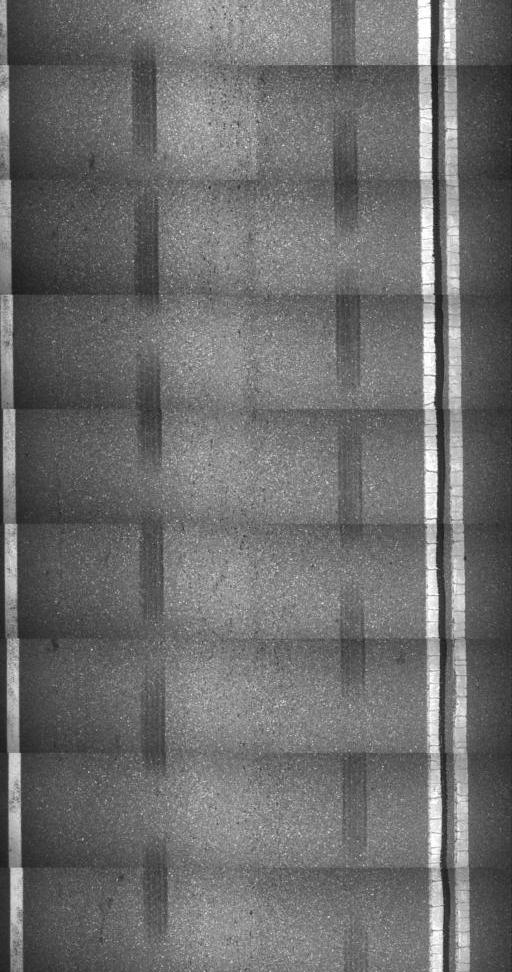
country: US
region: Vermont
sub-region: Windham County
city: Brattleboro
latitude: 42.8272
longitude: -72.5738
